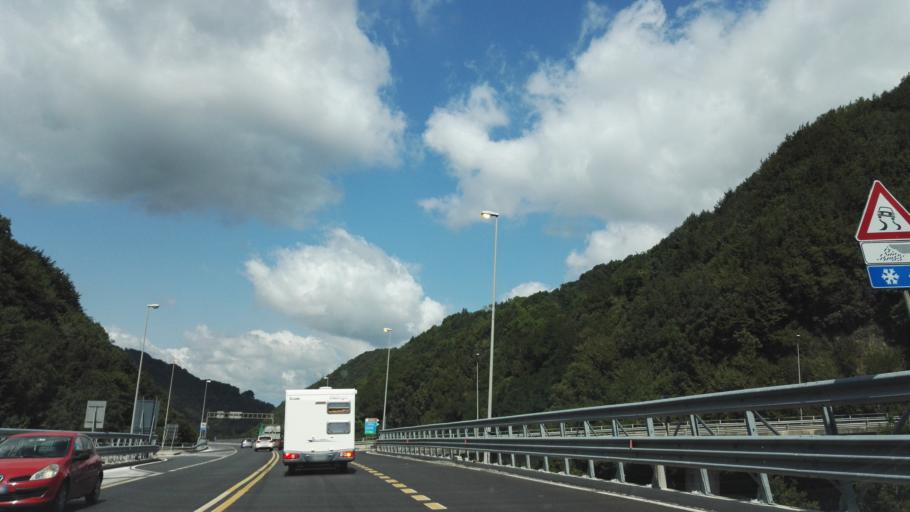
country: IT
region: Calabria
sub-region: Provincia di Reggio Calabria
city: Amato
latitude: 38.4025
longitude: 16.1613
